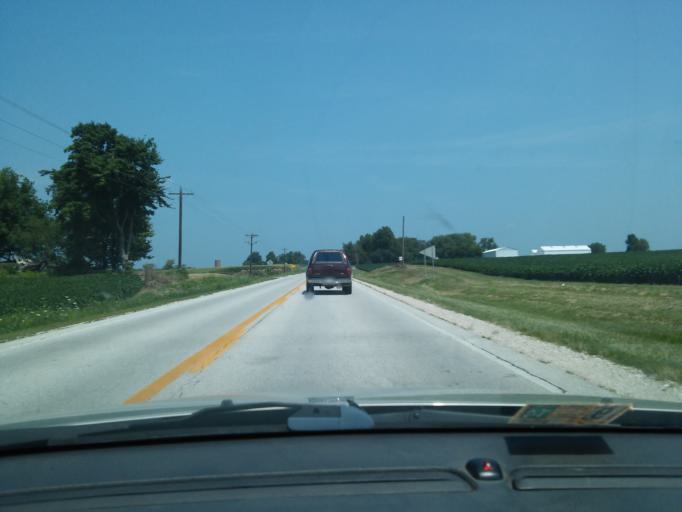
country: US
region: Illinois
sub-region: Pike County
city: Pittsfield
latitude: 39.5501
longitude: -90.9165
